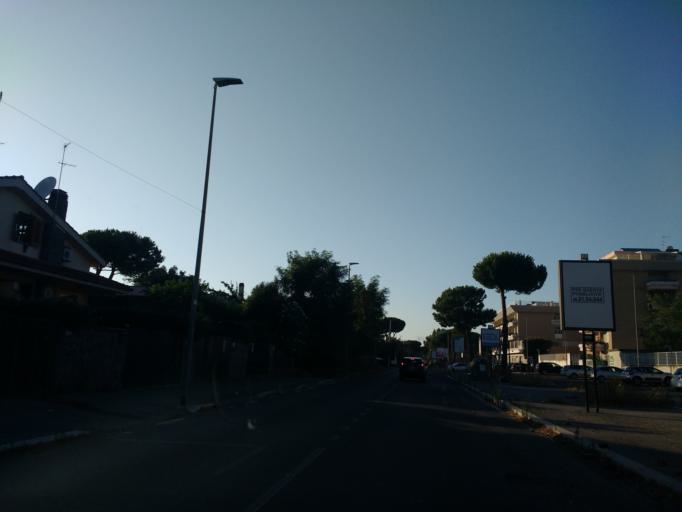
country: IT
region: Latium
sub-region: Citta metropolitana di Roma Capitale
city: Vitinia
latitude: 41.7746
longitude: 12.3706
